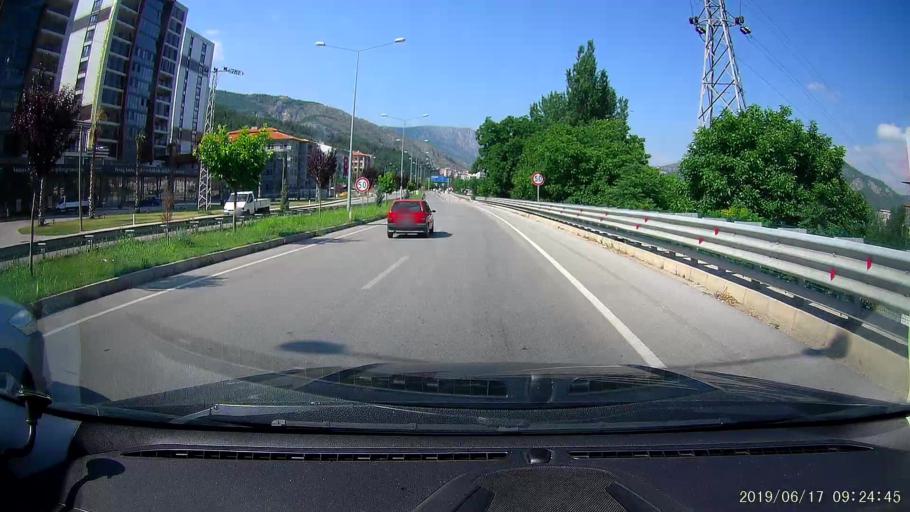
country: TR
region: Amasya
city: Amasya
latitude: 40.6704
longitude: 35.8538
